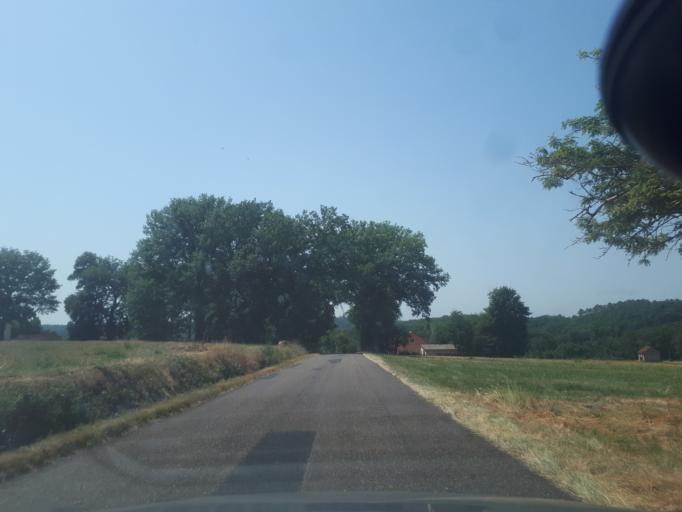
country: FR
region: Midi-Pyrenees
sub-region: Departement du Lot
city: Gourdon
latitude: 44.8068
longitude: 1.3744
